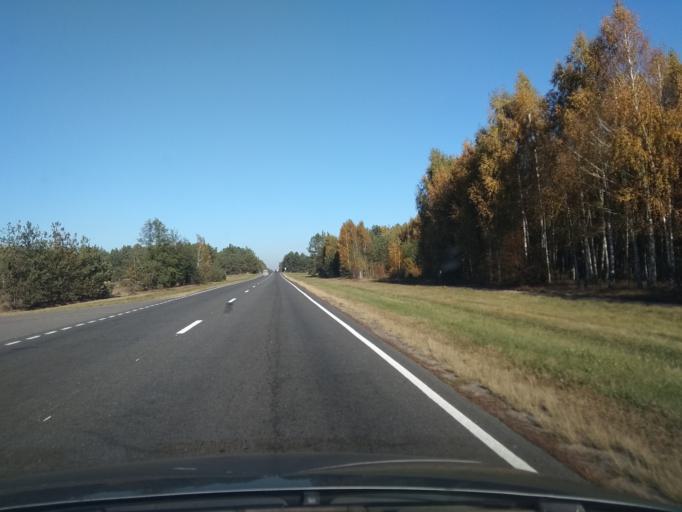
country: BY
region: Brest
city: Kobryn
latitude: 52.0701
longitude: 24.2835
